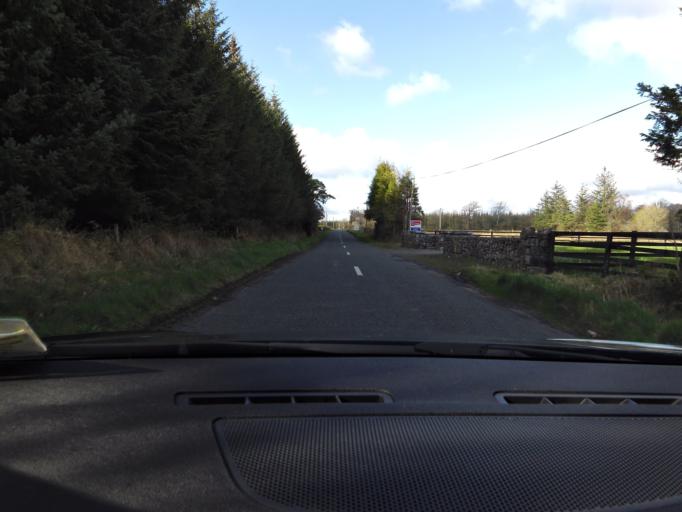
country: IE
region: Connaught
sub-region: County Galway
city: Athenry
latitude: 53.4562
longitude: -8.5501
